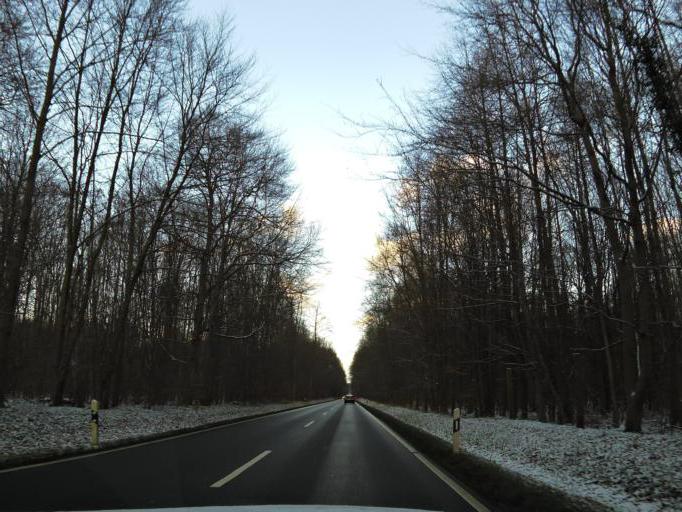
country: DE
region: Hesse
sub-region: Regierungsbezirk Darmstadt
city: Messel
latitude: 49.9101
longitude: 8.7084
